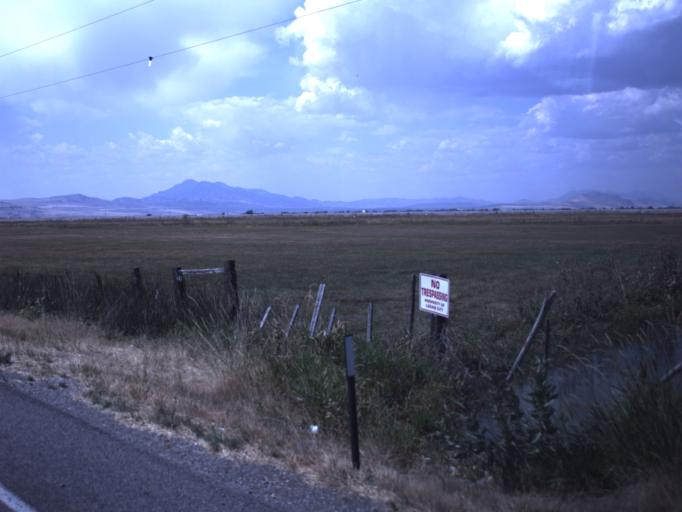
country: US
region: Utah
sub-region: Cache County
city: Logan
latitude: 41.7366
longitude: -111.8905
